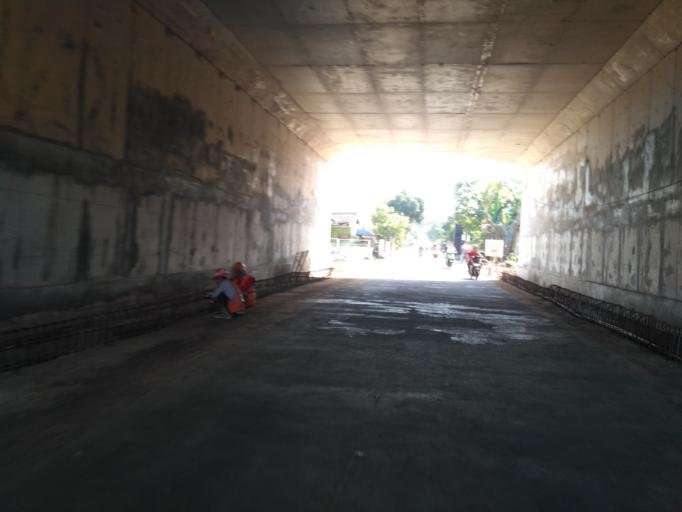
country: ID
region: East Java
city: Singosari
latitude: -7.9236
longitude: 112.6670
